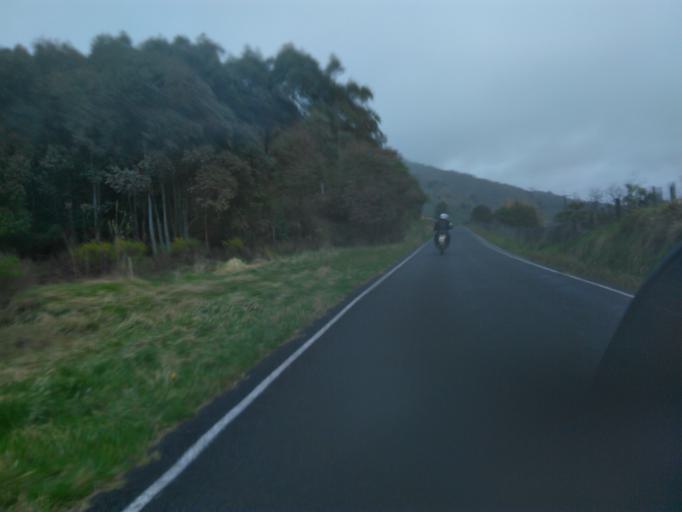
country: NZ
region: Gisborne
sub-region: Gisborne District
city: Gisborne
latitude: -38.6678
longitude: 177.7152
